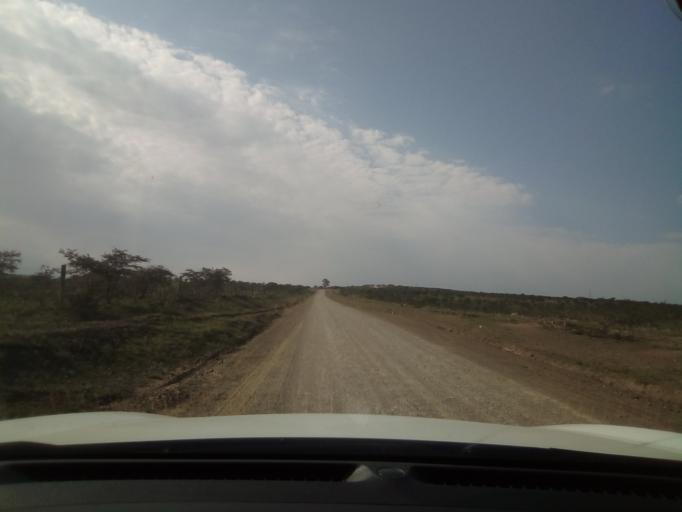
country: ZA
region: Eastern Cape
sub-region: Buffalo City Metropolitan Municipality
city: Bhisho
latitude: -32.9883
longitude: 27.2427
